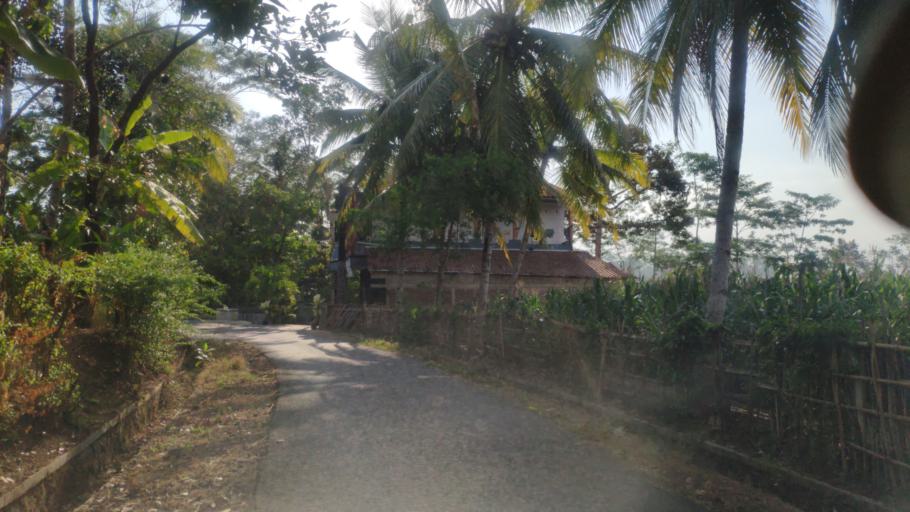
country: ID
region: Central Java
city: Wonosobo
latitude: -7.4031
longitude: 109.6624
